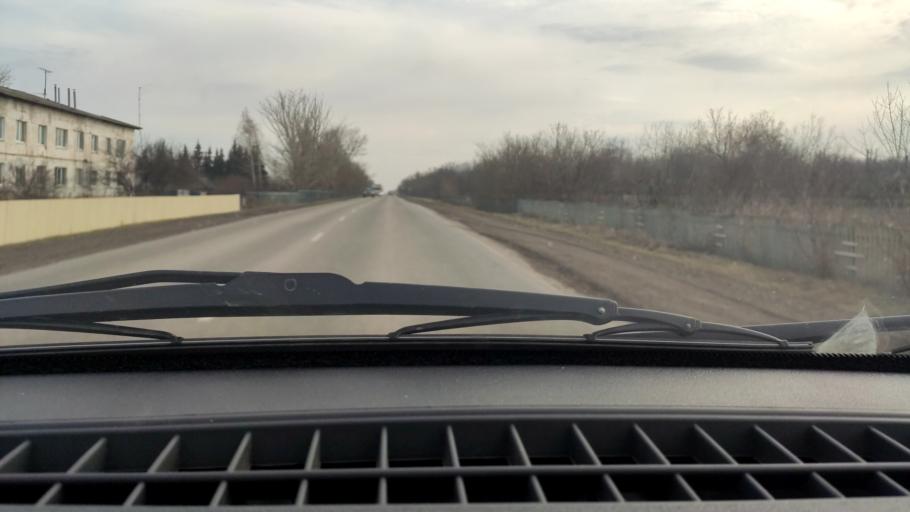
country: RU
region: Bashkortostan
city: Davlekanovo
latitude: 54.2932
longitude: 55.1235
